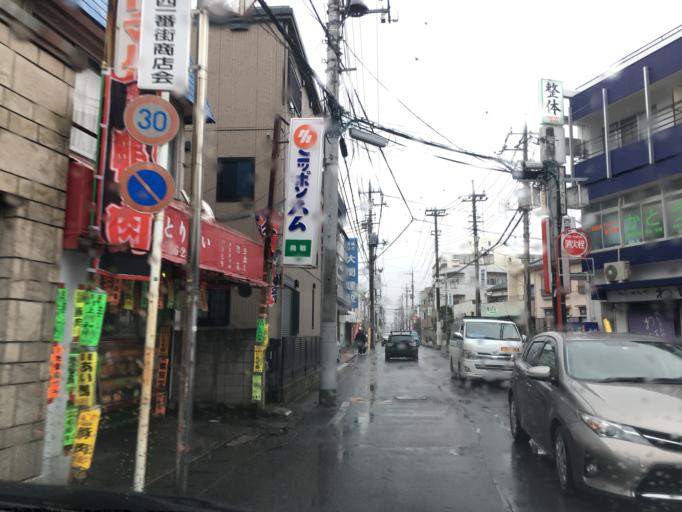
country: JP
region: Saitama
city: Koshigaya
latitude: 35.8897
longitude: 139.7850
